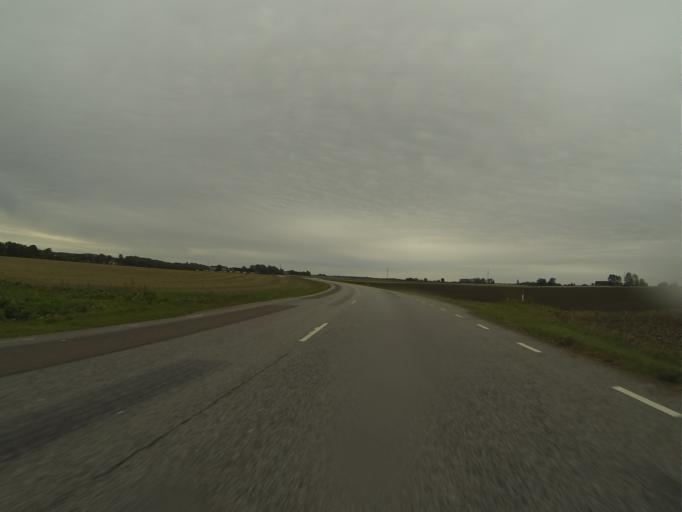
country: SE
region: Skane
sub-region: Svedala Kommun
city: Klagerup
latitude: 55.6297
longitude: 13.2946
